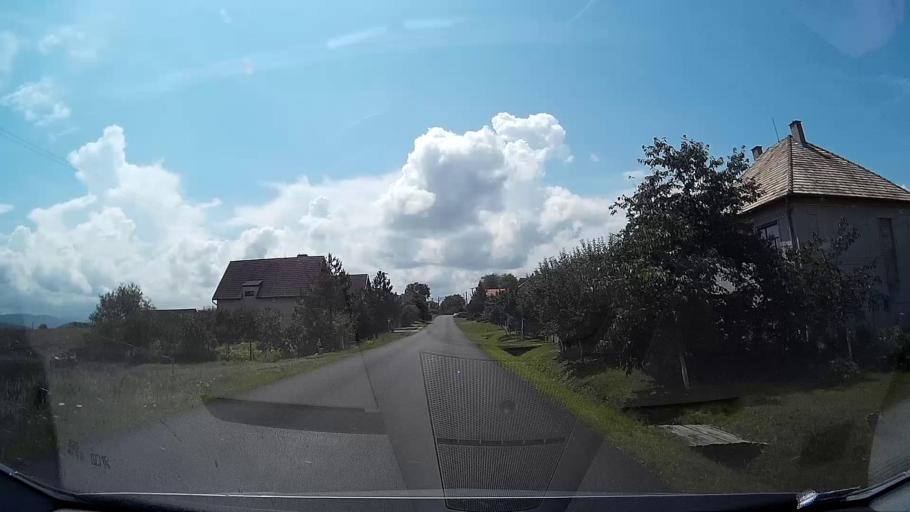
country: SK
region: Banskobystricky
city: Fil'akovo
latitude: 48.3102
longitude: 19.8034
